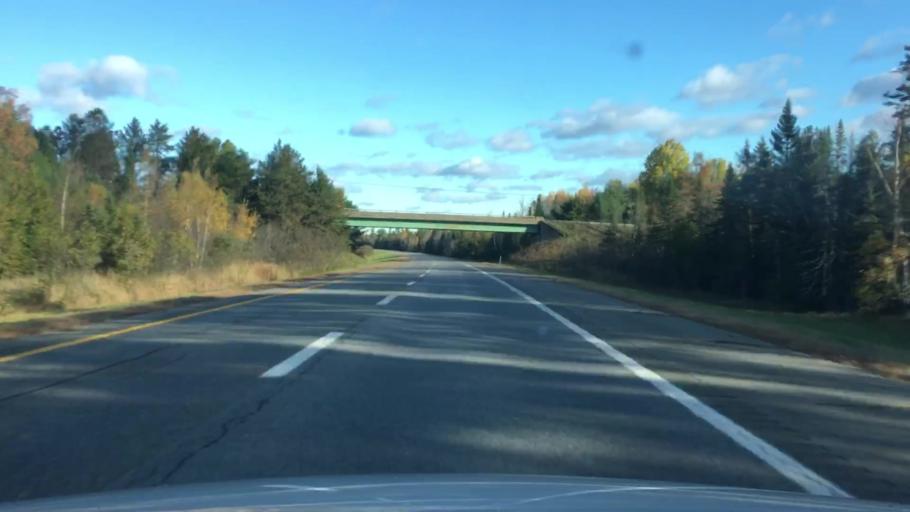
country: US
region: Maine
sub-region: Penobscot County
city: Greenbush
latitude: 45.0509
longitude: -68.6873
